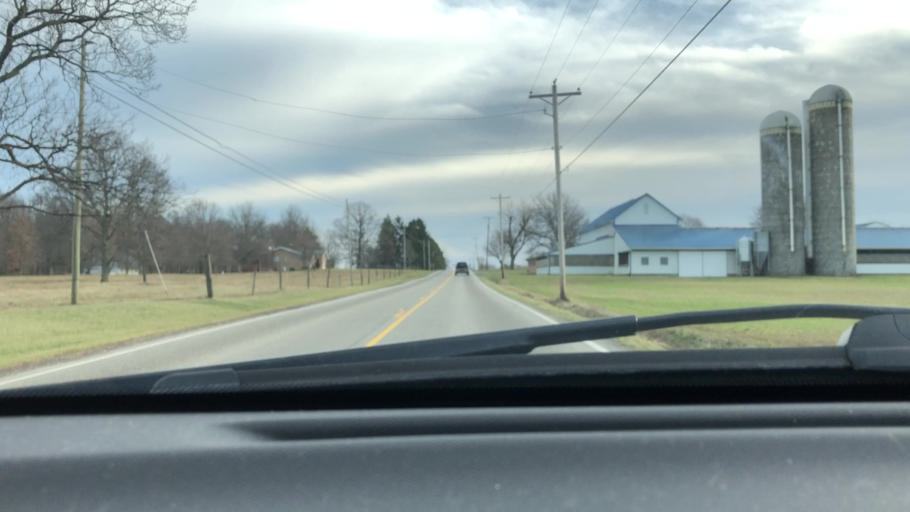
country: US
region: Ohio
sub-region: Wayne County
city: Dalton
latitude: 40.7617
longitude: -81.7452
